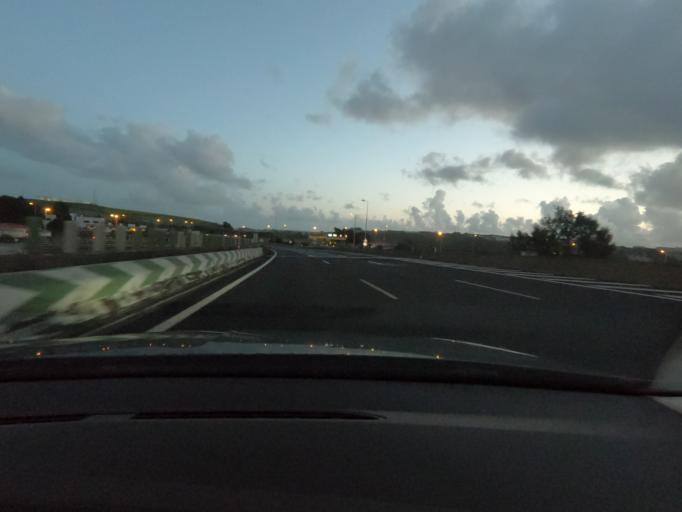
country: PT
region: Lisbon
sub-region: Oeiras
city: Barcarena
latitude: 38.7446
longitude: -9.2753
